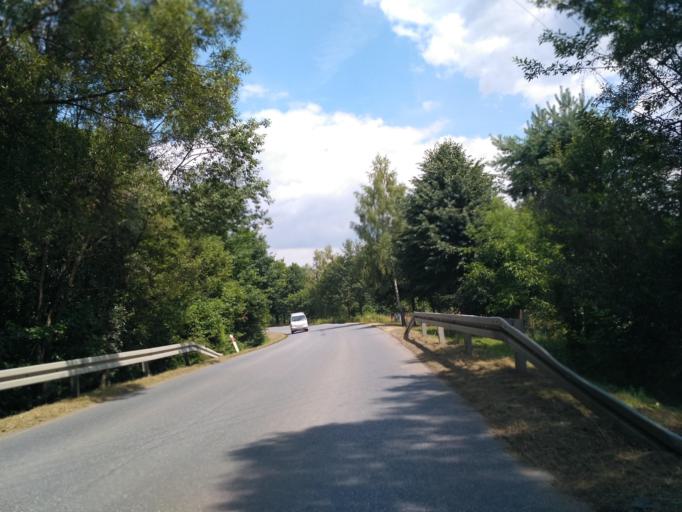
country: PL
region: Subcarpathian Voivodeship
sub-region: Powiat debicki
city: Pilzno
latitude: 50.0077
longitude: 21.2870
